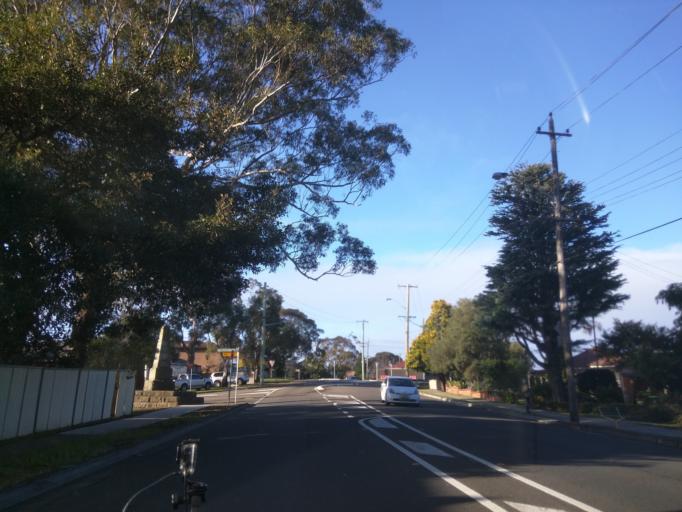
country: AU
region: New South Wales
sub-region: Hurstville
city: Lugarno
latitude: -33.9812
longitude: 151.0462
